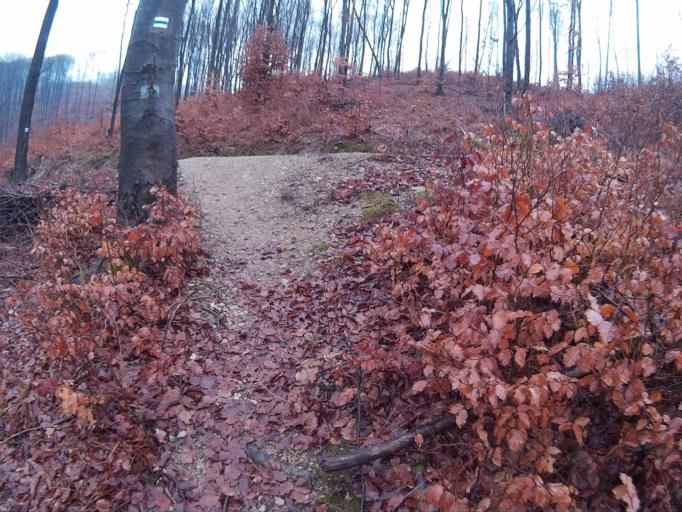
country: HU
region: Borsod-Abauj-Zemplen
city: Sarospatak
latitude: 48.4190
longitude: 21.5566
